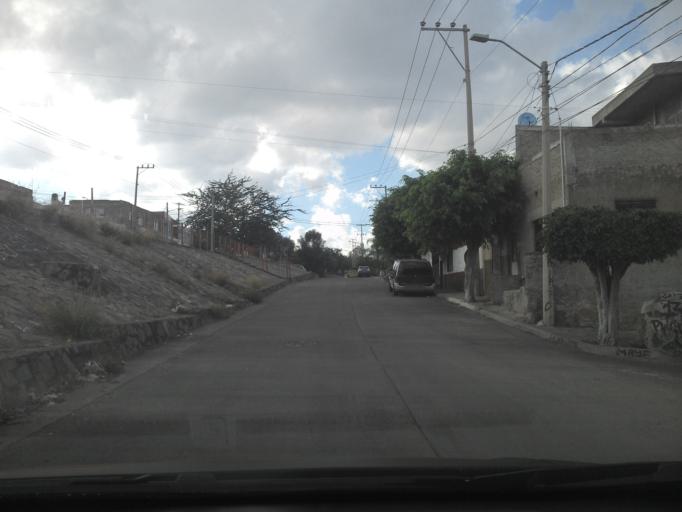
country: MX
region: Jalisco
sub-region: Tlajomulco de Zuniga
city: Altus Bosques
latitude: 20.6161
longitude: -103.3690
